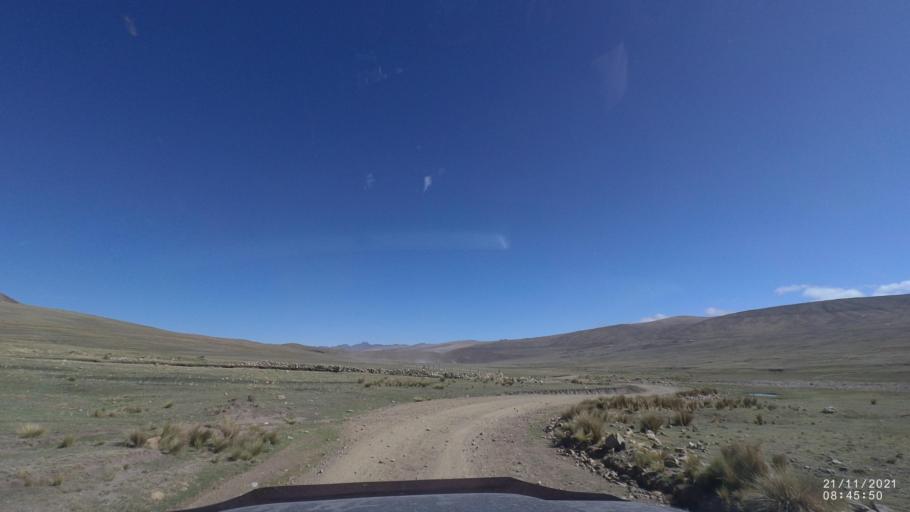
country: BO
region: Cochabamba
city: Cochabamba
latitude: -17.2459
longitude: -66.2323
